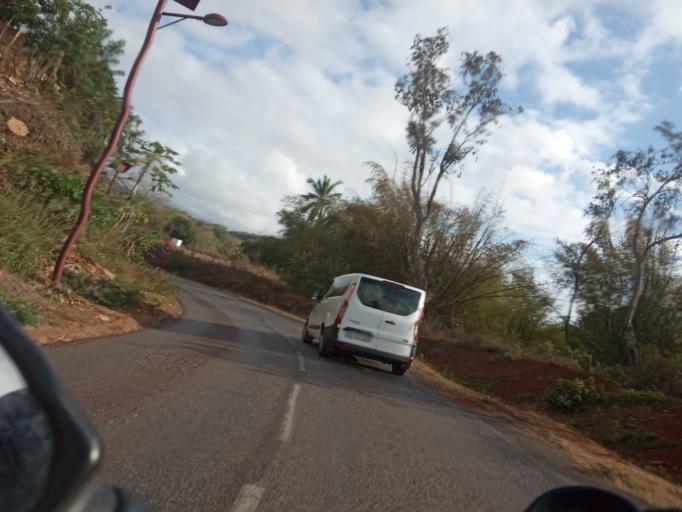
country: YT
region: Dembeni
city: Dembeni
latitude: -12.8679
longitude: 45.1991
